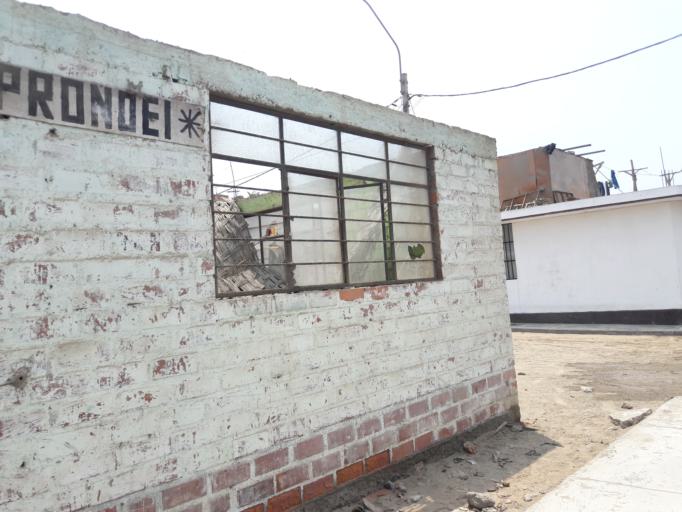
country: PE
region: Lima
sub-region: Lima
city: Santa Rosa
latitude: -11.7698
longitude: -77.1615
